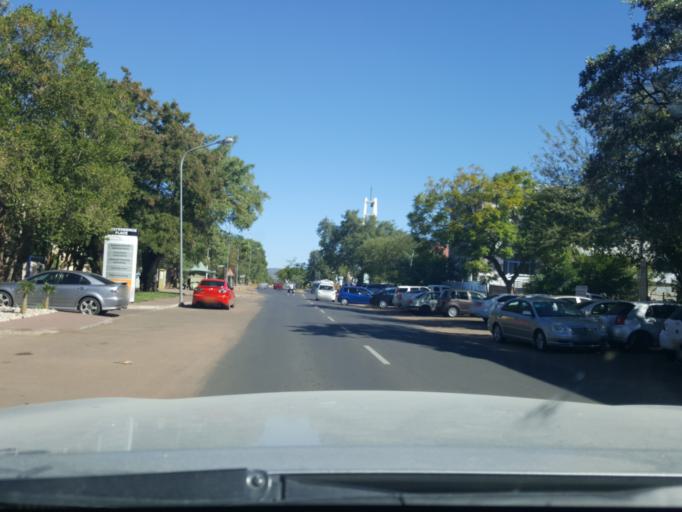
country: BW
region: South East
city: Gaborone
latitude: -24.6557
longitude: 25.9191
